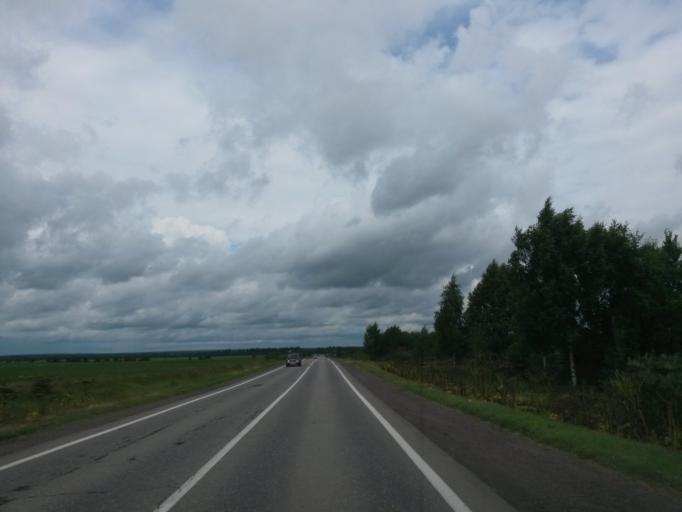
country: RU
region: Jaroslavl
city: Yaroslavl
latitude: 57.7717
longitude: 39.8543
